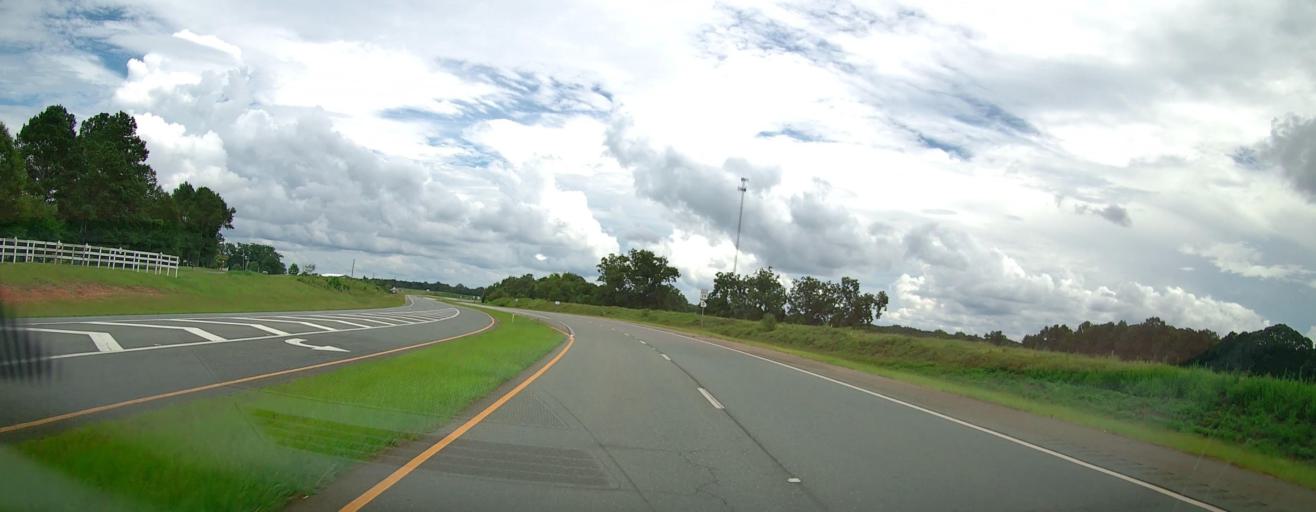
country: US
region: Georgia
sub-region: Schley County
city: Ellaville
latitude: 32.2265
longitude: -84.2922
